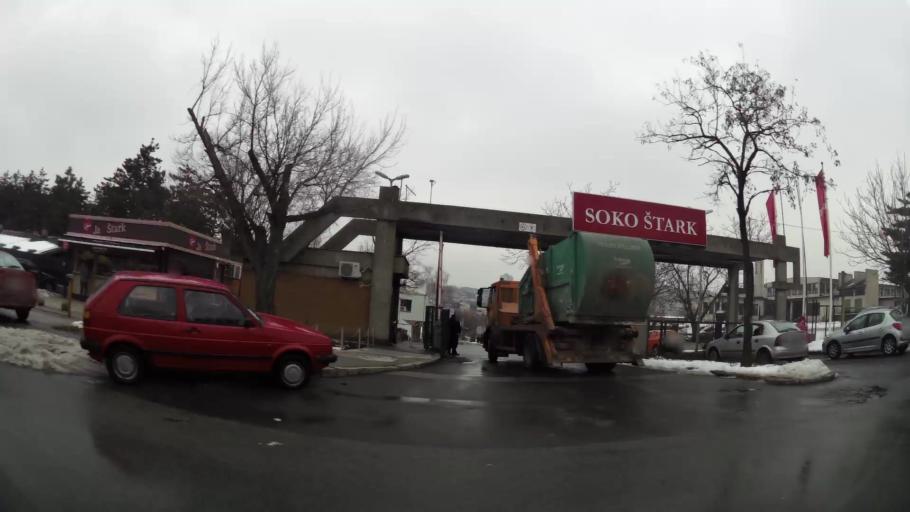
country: RS
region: Central Serbia
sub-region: Belgrade
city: Vozdovac
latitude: 44.7645
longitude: 20.4884
